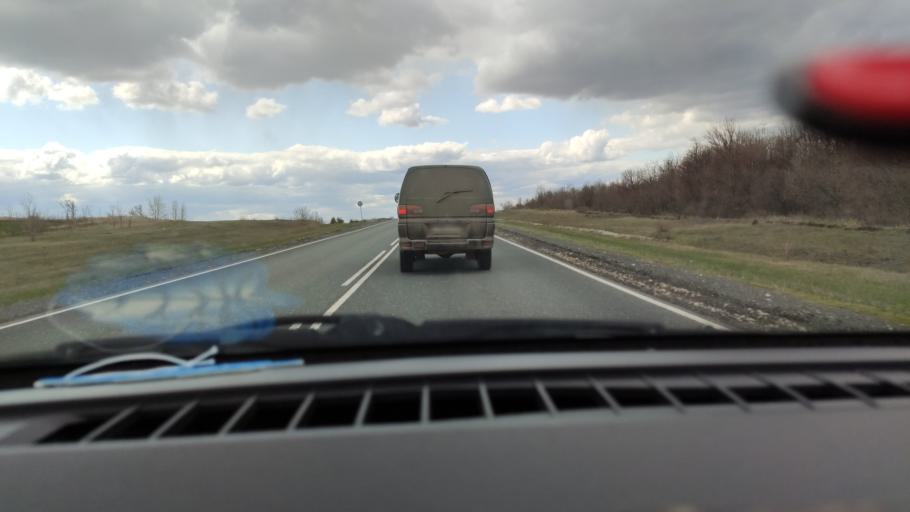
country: RU
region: Saratov
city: Balakovo
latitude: 52.1885
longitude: 47.8507
